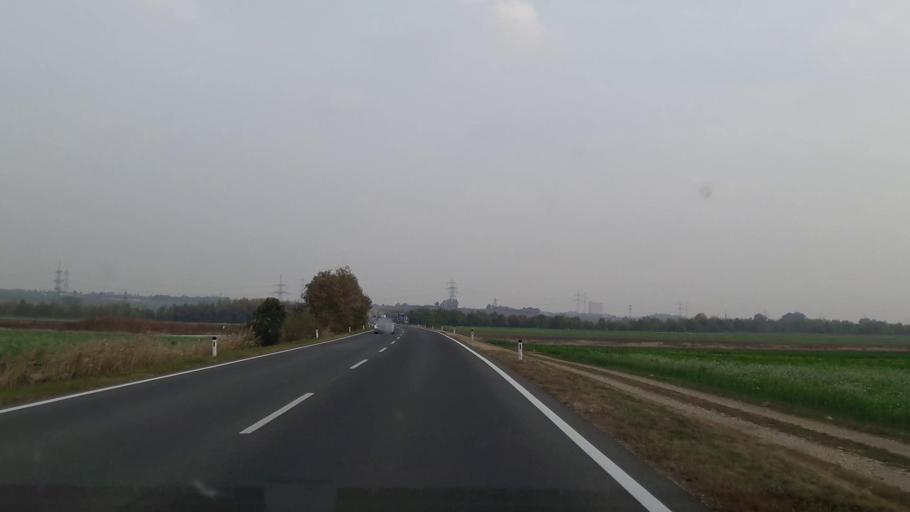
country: AT
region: Burgenland
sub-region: Politischer Bezirk Neusiedl am See
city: Parndorf
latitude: 48.0078
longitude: 16.8259
